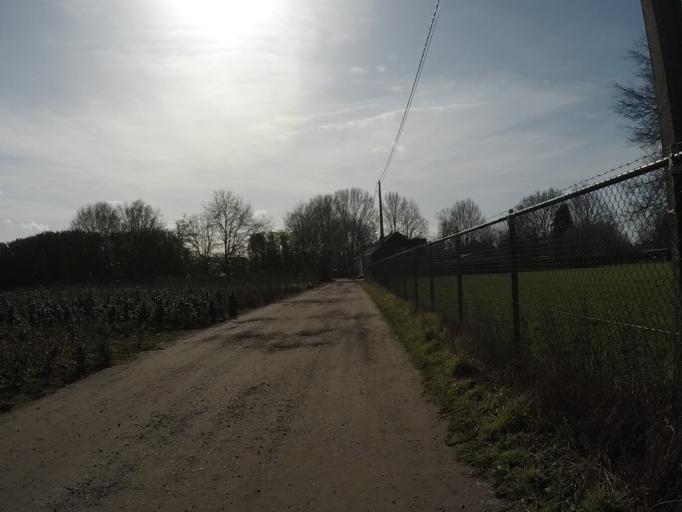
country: BE
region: Flanders
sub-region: Provincie Antwerpen
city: Ranst
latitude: 51.2038
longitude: 4.5467
